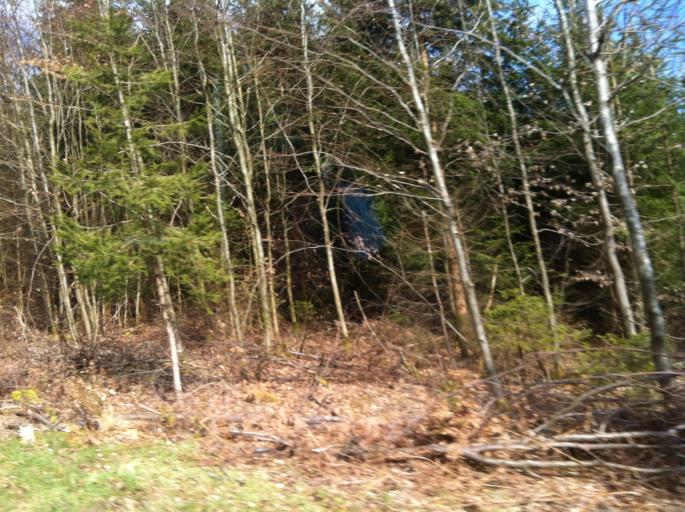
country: DE
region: Baden-Wuerttemberg
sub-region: Karlsruhe Region
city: Mudau
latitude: 49.5019
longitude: 9.2122
